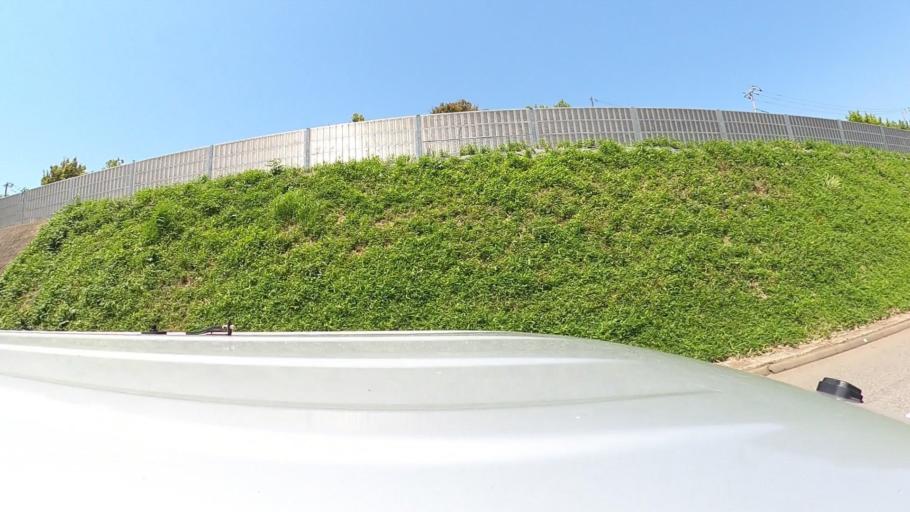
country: JP
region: Ibaraki
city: Mitsukaido
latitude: 36.0000
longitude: 140.0368
